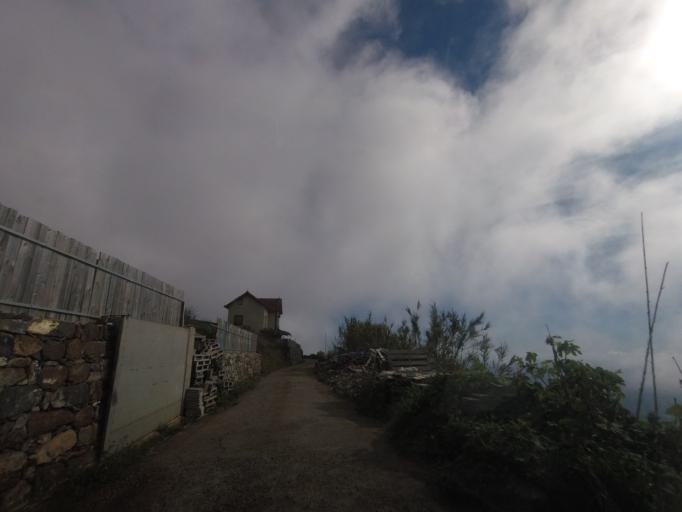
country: PT
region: Madeira
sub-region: Calheta
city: Faja da Ovelha
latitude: 32.7593
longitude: -17.2197
